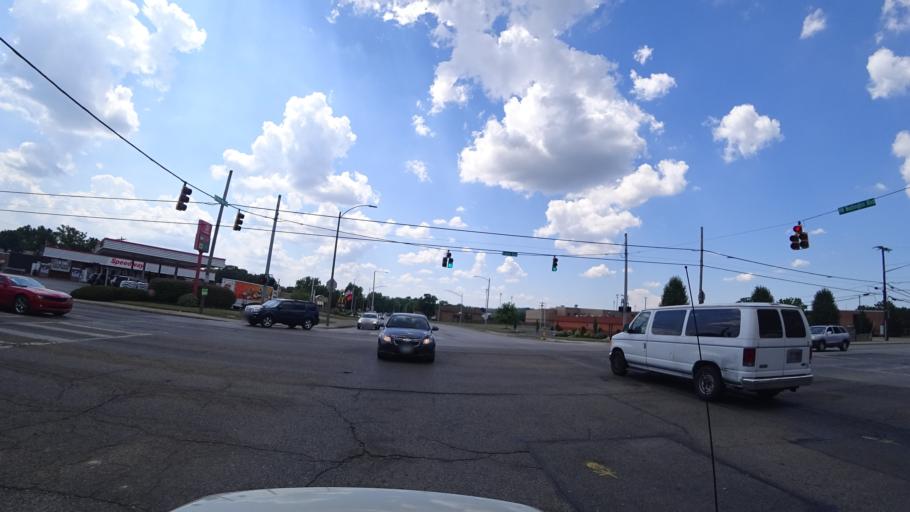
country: US
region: Ohio
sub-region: Butler County
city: Hamilton
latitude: 39.4235
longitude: -84.5768
